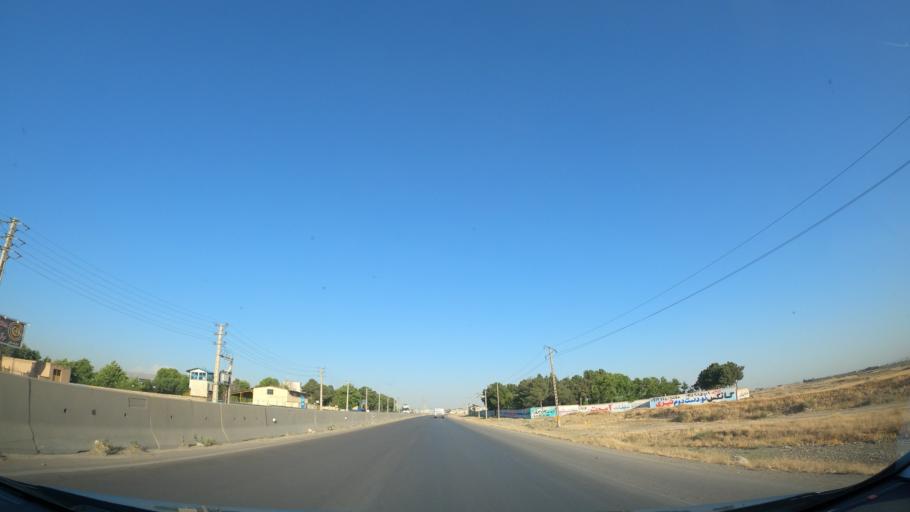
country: IR
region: Alborz
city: Hashtgerd
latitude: 35.9221
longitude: 50.7445
